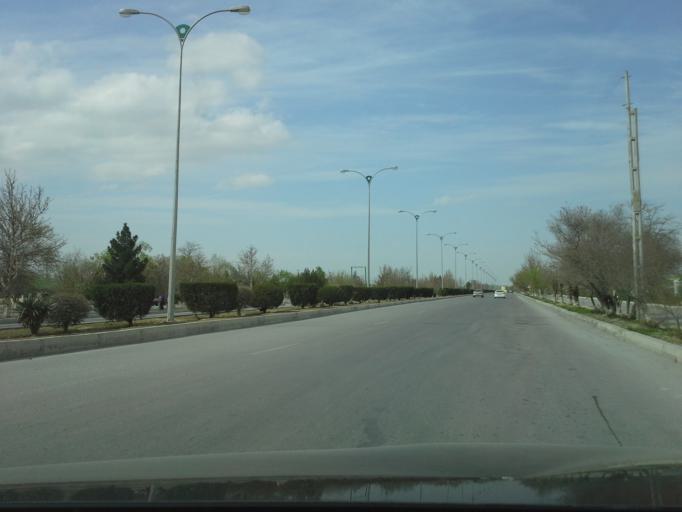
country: TM
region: Ahal
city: Abadan
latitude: 38.0359
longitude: 58.1884
